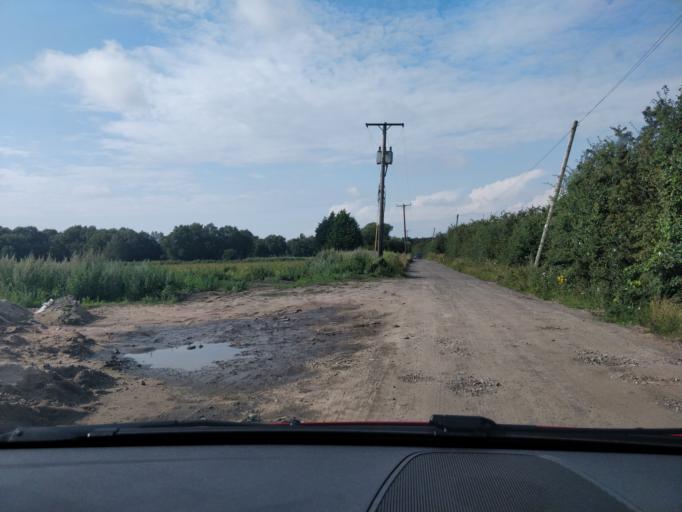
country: GB
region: England
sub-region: Sefton
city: Southport
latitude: 53.6489
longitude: -2.9557
